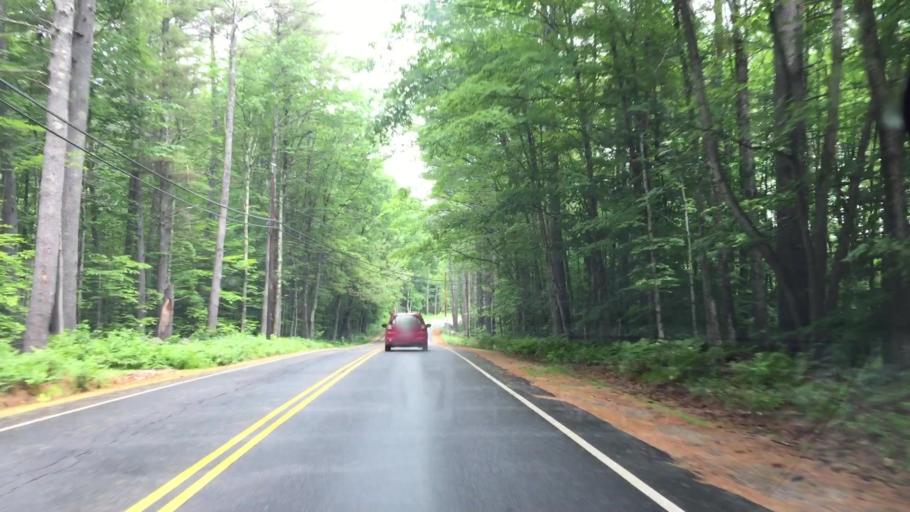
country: US
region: New Hampshire
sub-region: Carroll County
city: Sandwich
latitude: 43.8026
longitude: -71.4428
